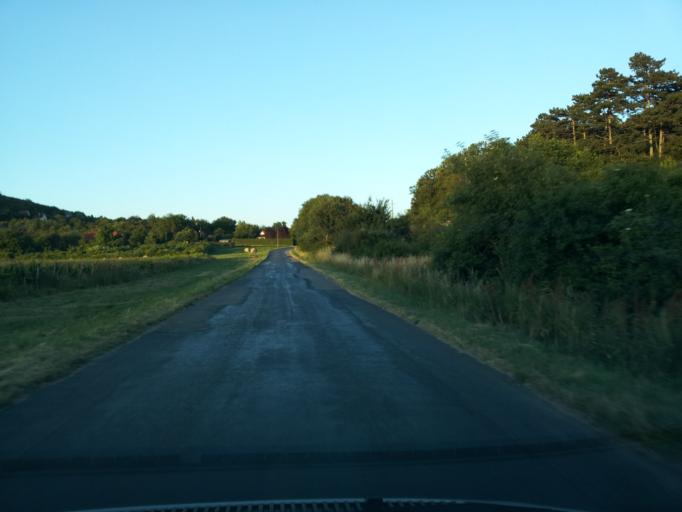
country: HU
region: Veszprem
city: Szentkiralyszabadja
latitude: 47.0148
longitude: 17.9693
